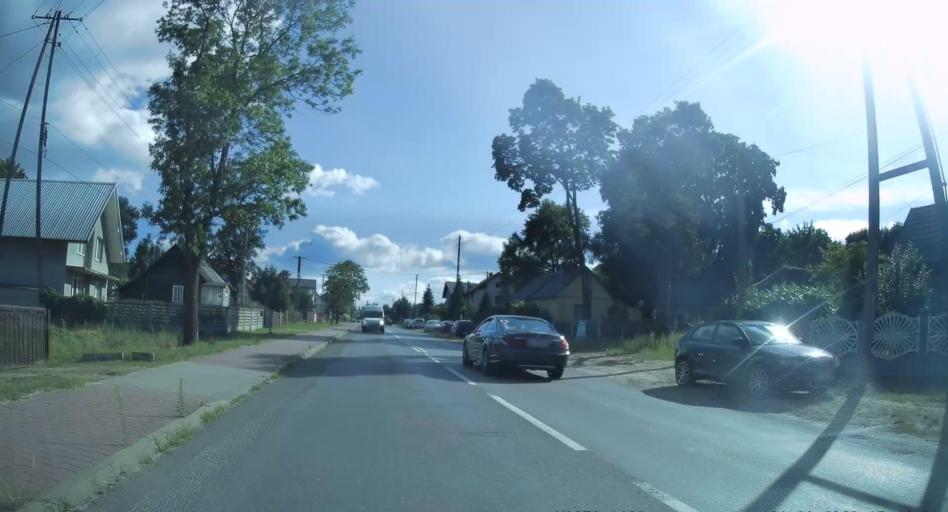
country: PL
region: Swietokrzyskie
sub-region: Powiat skarzyski
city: Suchedniow
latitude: 51.0279
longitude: 20.8374
